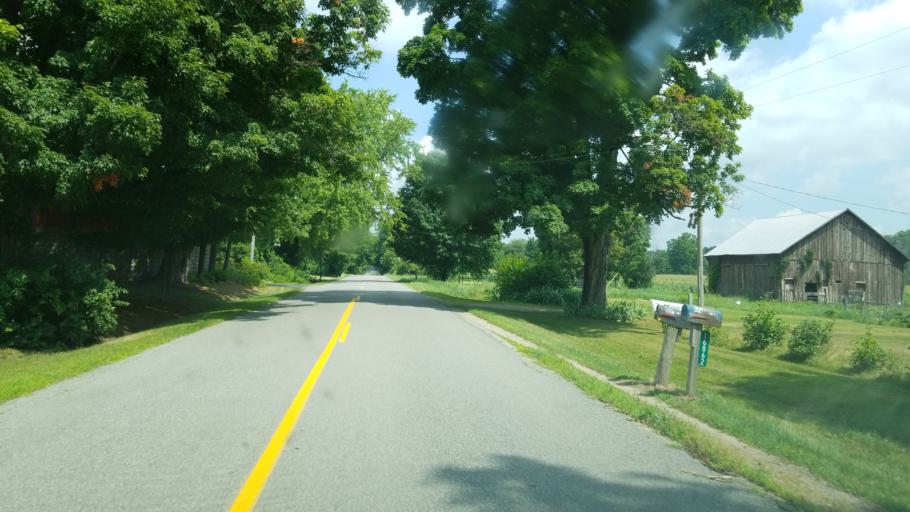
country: US
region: Michigan
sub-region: Kent County
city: Cedar Springs
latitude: 43.2722
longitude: -85.5114
